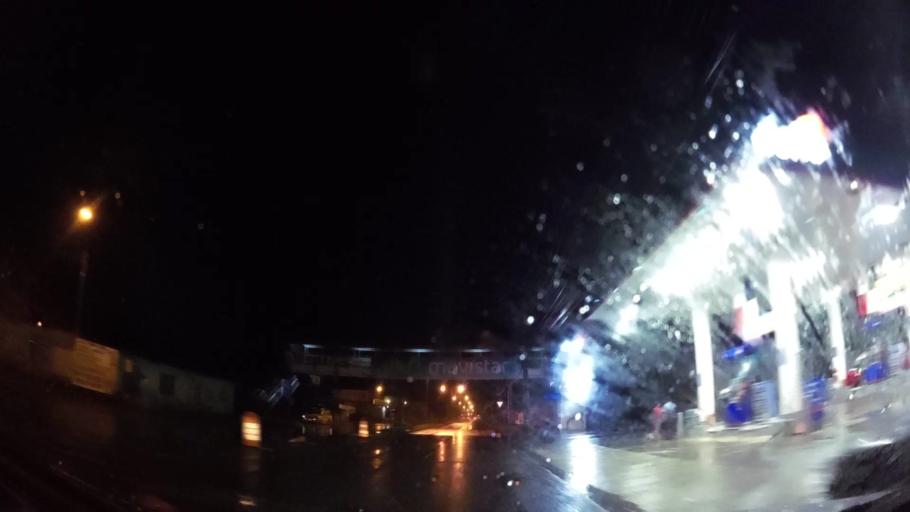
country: PA
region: Cocle
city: Rio Hato
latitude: 8.3789
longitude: -80.1646
